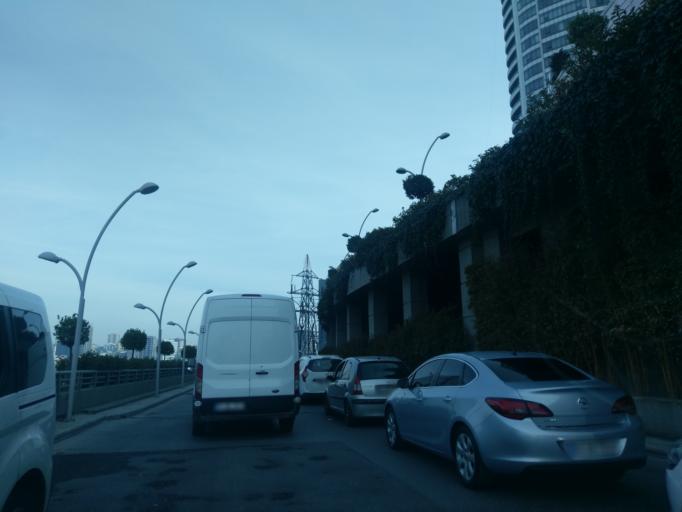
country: TR
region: Istanbul
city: Mahmutbey
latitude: 41.0642
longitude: 28.8094
